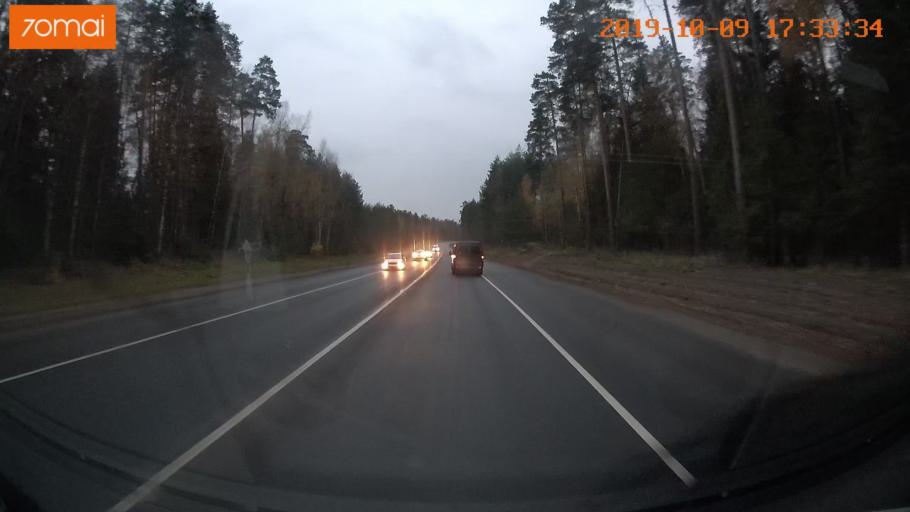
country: RU
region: Ivanovo
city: Bogorodskoye
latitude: 57.1162
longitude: 41.0188
